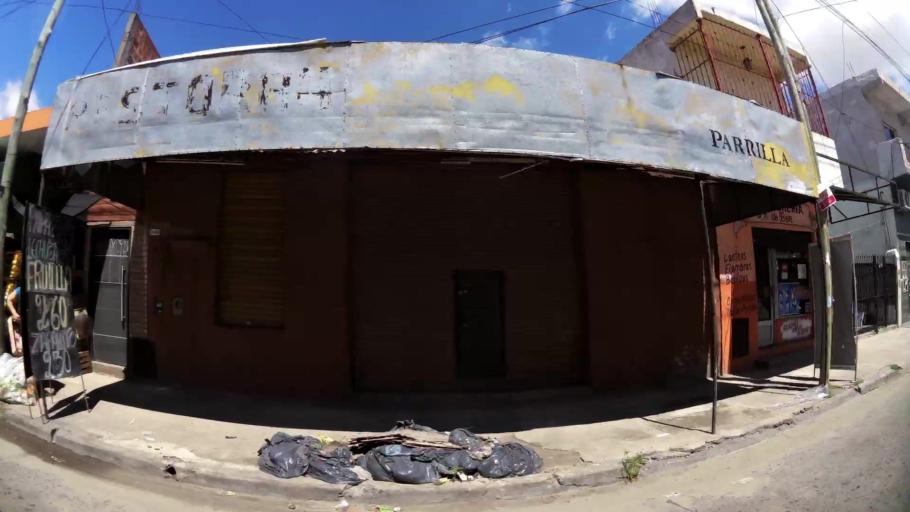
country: AR
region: Buenos Aires
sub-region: Partido de Lanus
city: Lanus
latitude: -34.6968
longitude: -58.4221
